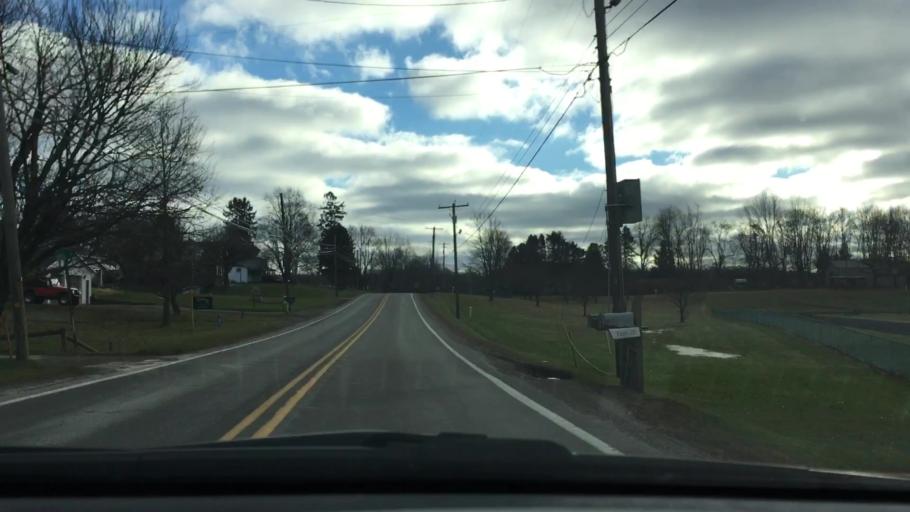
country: US
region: Pennsylvania
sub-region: Armstrong County
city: Orchard Hills
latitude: 40.6083
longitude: -79.4739
